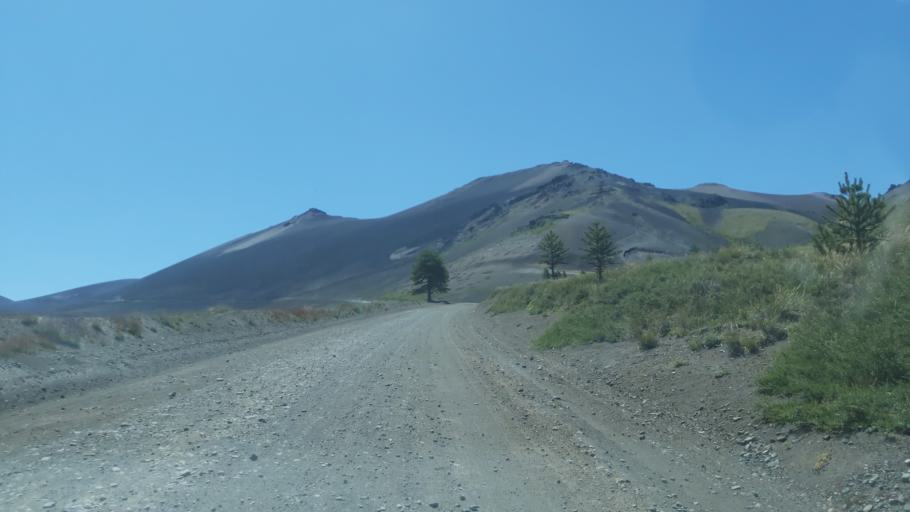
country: CL
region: Araucania
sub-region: Provincia de Cautin
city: Vilcun
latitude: -38.4177
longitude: -71.5440
